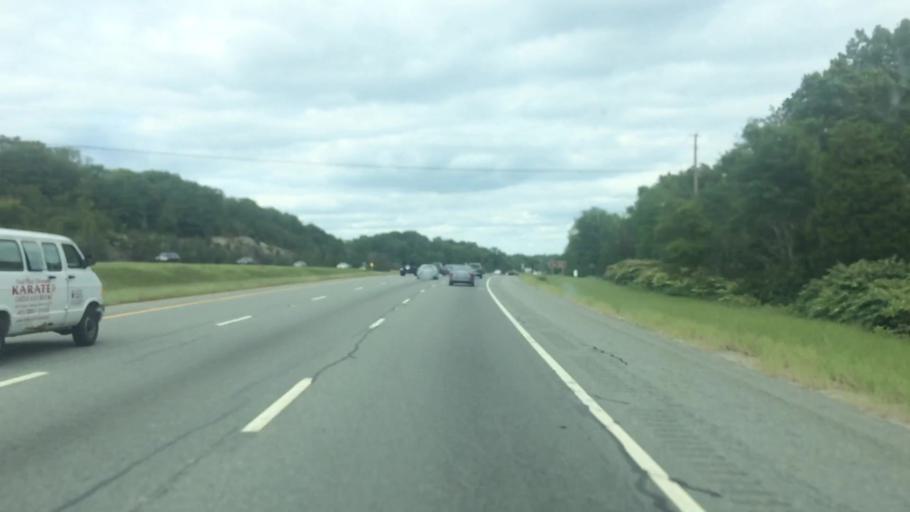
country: US
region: Rhode Island
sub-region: Providence County
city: Smithfield
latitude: 41.9300
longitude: -71.5021
